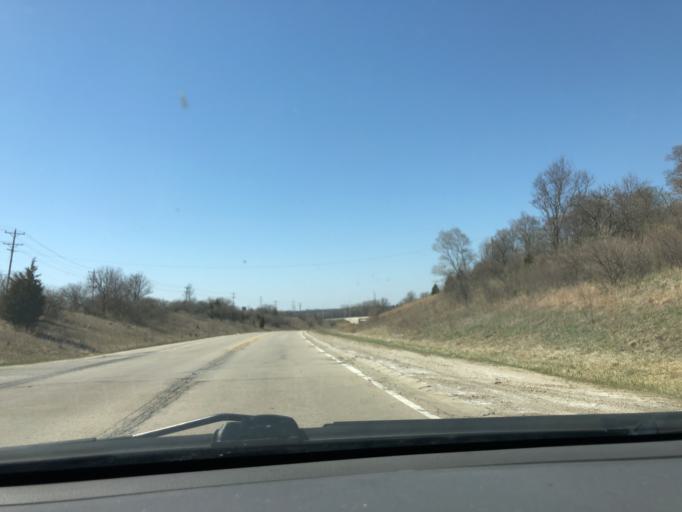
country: US
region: Illinois
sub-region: Kane County
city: Hampshire
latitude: 42.1388
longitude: -88.5040
